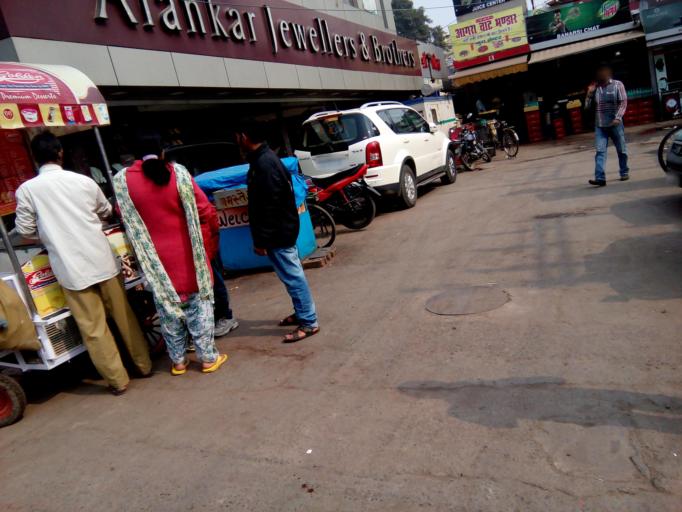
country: IN
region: Bihar
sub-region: Patna
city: Patna
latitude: 25.6151
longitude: 85.1526
